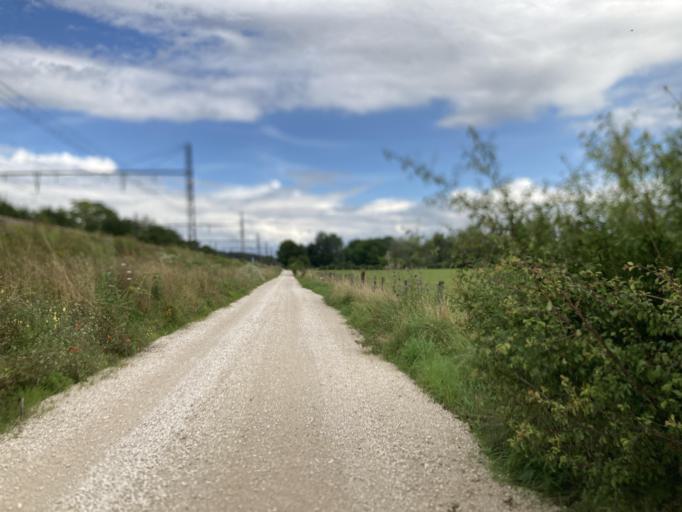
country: FR
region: Bourgogne
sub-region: Departement de la Cote-d'Or
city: Montbard
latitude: 47.6171
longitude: 4.3734
